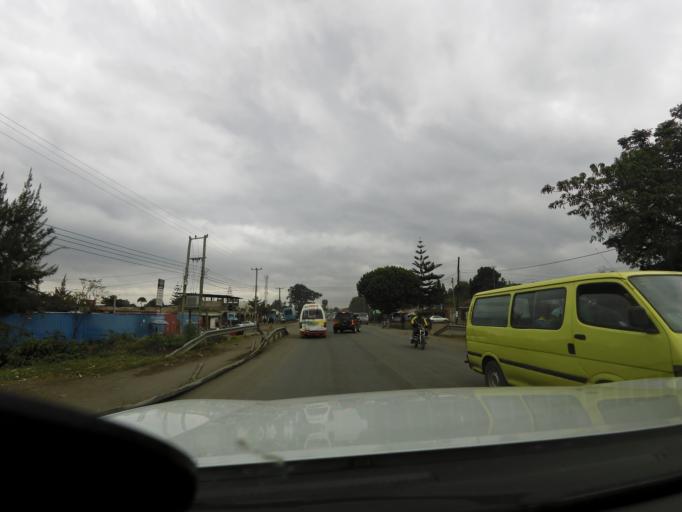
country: TZ
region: Arusha
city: Arusha
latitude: -3.3630
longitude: 36.6732
